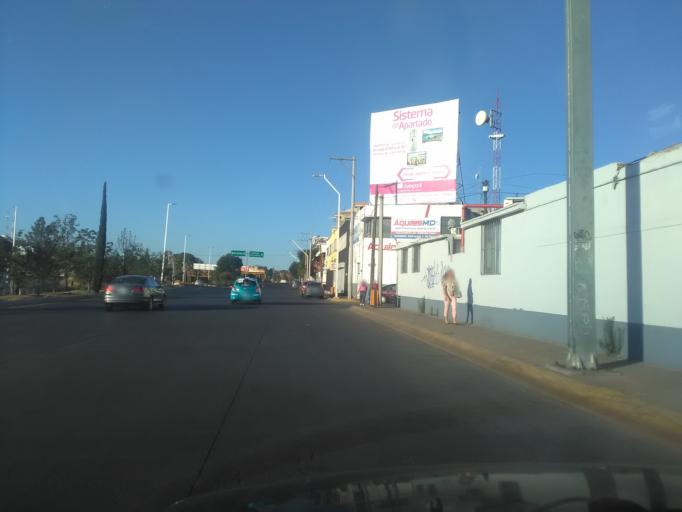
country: MX
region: Durango
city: Victoria de Durango
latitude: 24.0337
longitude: -104.6848
